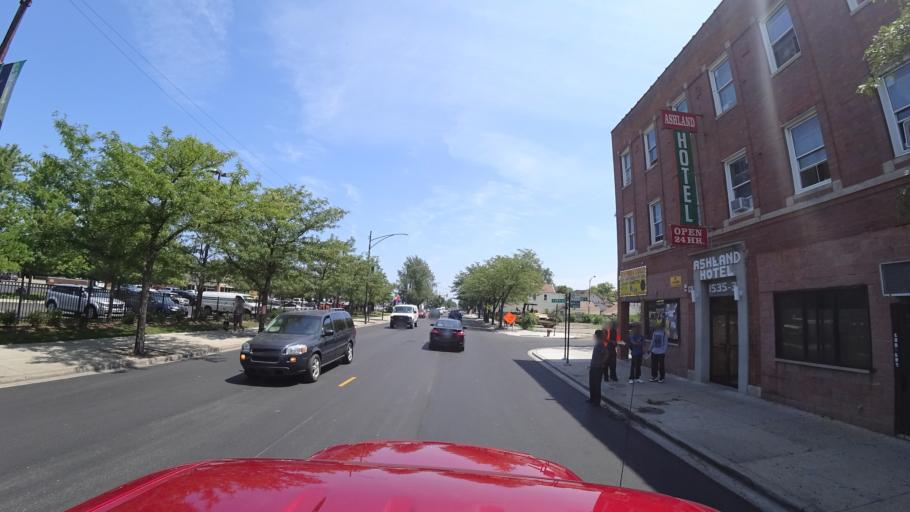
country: US
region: Illinois
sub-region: Cook County
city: Chicago
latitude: 41.8086
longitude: -87.6641
